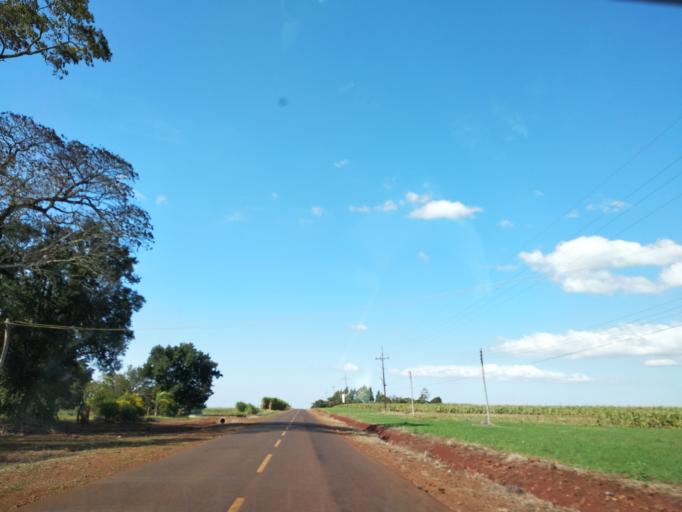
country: PY
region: Itapua
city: Hohenau
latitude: -27.0702
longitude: -55.7199
